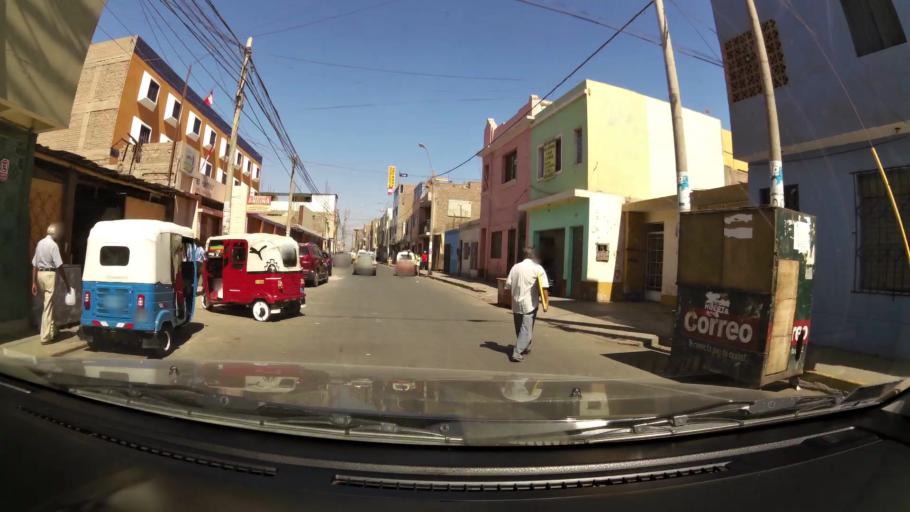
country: PE
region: Ica
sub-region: Provincia de Ica
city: Ica
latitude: -14.0600
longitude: -75.7286
